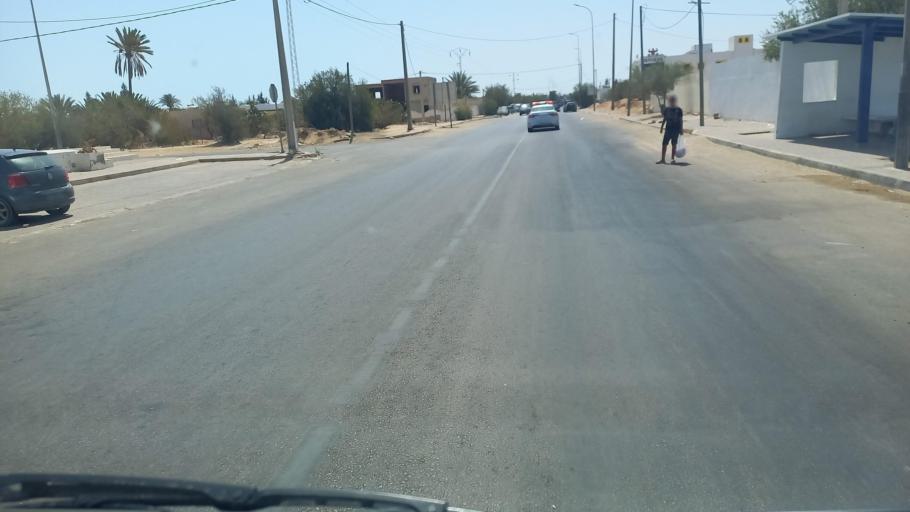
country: TN
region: Madanin
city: Houmt Souk
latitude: 33.7991
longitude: 10.8842
